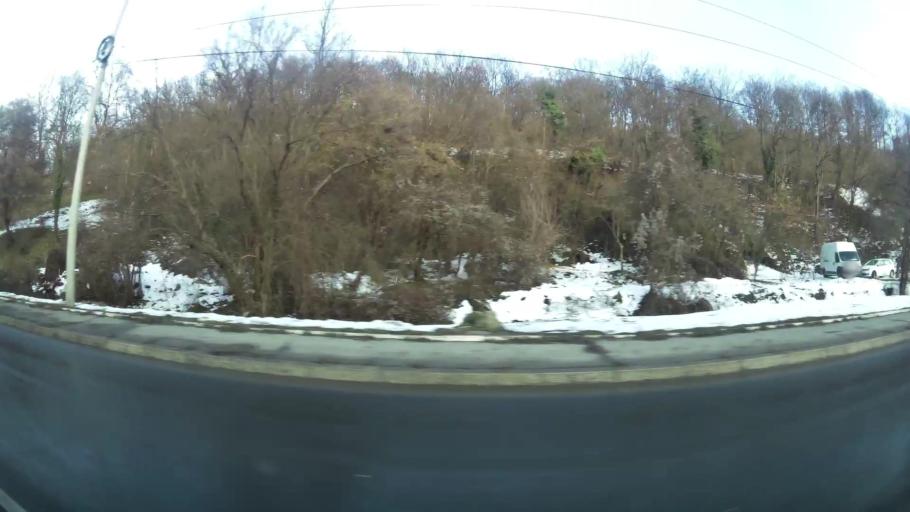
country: RS
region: Central Serbia
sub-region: Belgrade
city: Rakovica
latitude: 44.7307
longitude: 20.4476
